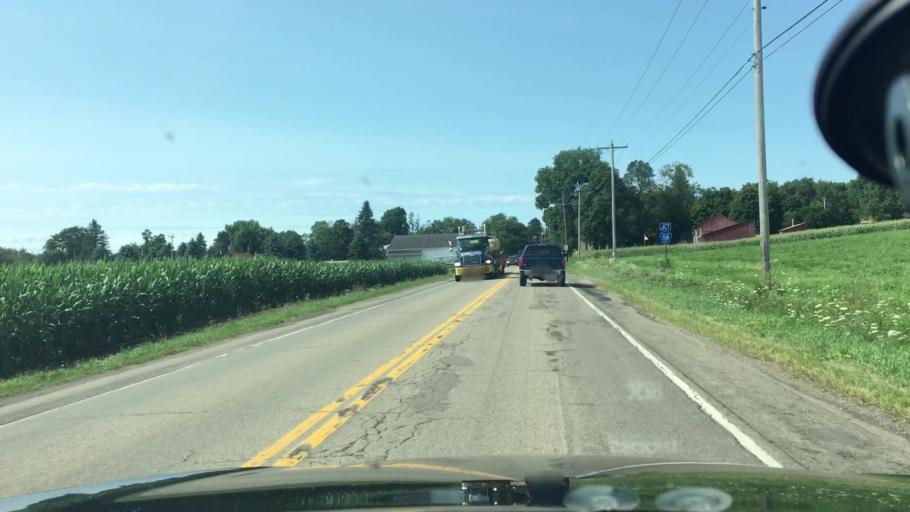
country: US
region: New York
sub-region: Chautauqua County
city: Brocton
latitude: 42.3134
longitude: -79.3547
